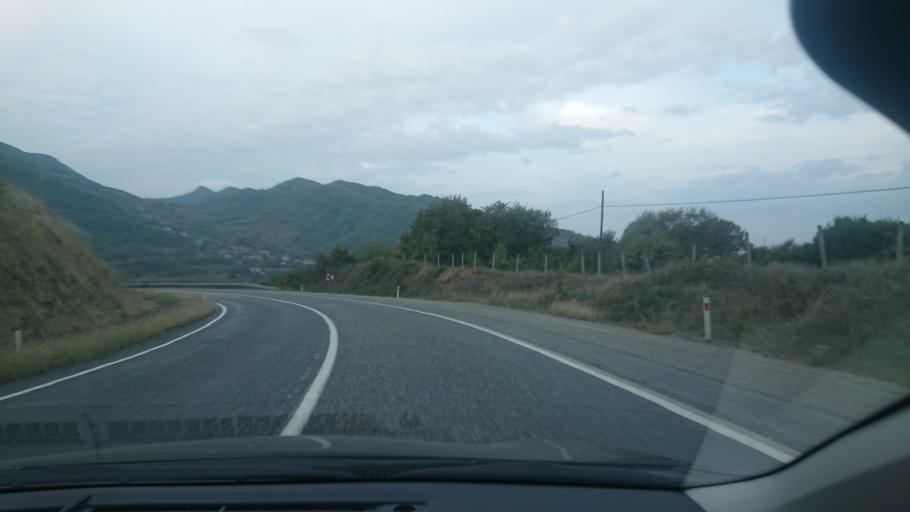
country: TR
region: Zonguldak
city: Gokcebey
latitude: 41.2841
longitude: 32.1576
